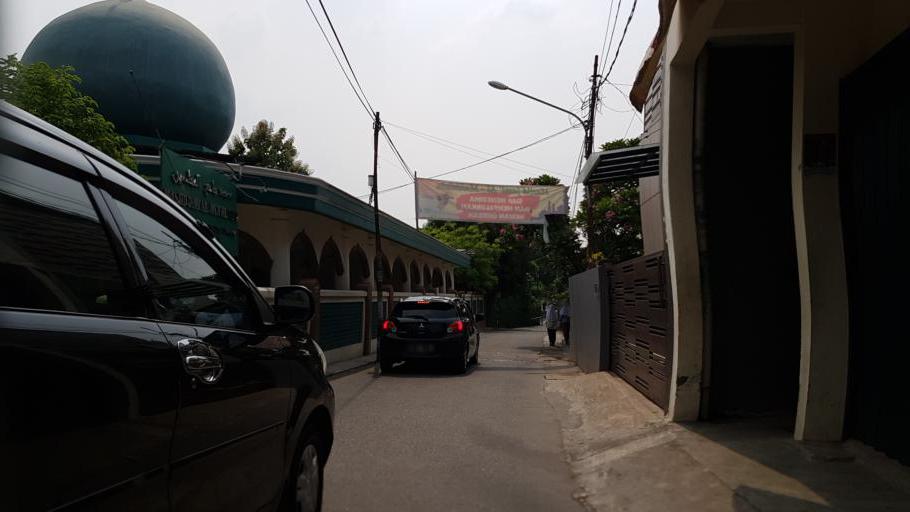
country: ID
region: West Java
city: Pamulang
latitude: -6.3295
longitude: 106.7880
